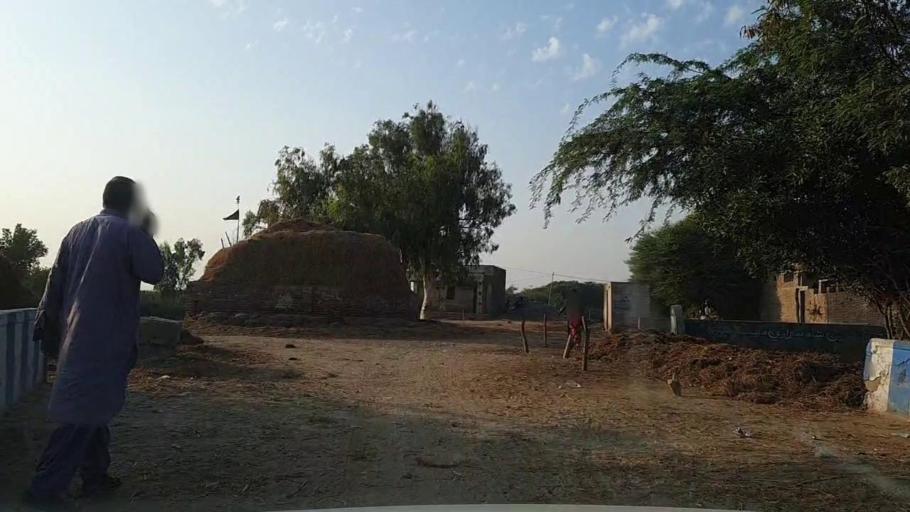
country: PK
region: Sindh
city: Daro Mehar
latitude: 24.7770
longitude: 68.1951
